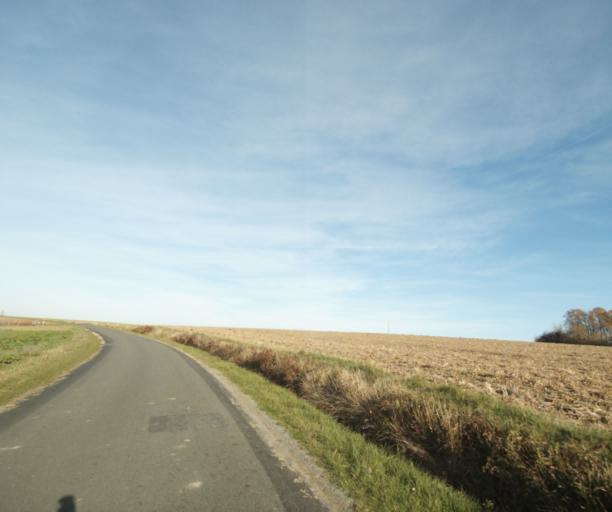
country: FR
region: Poitou-Charentes
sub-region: Departement de la Charente-Maritime
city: Chaniers
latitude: 45.7159
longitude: -0.5296
